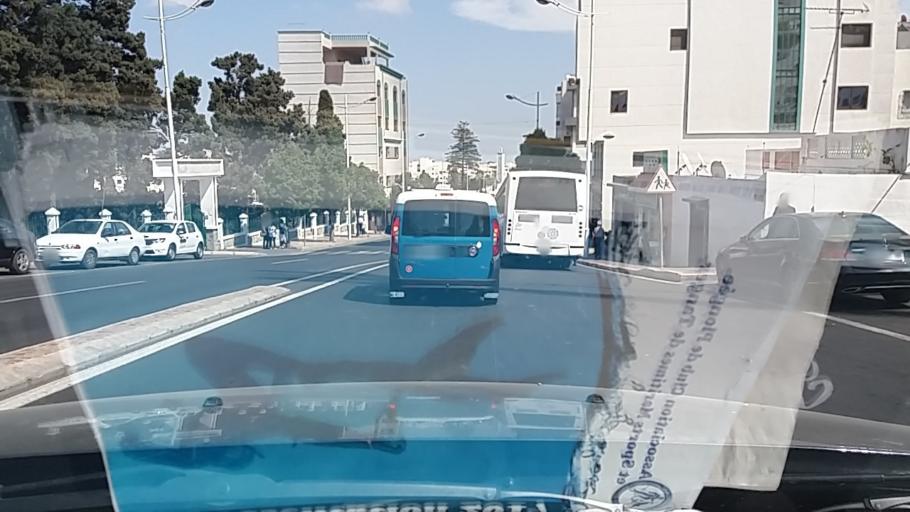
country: MA
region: Tanger-Tetouan
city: Tetouan
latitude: 35.5717
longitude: -5.3590
